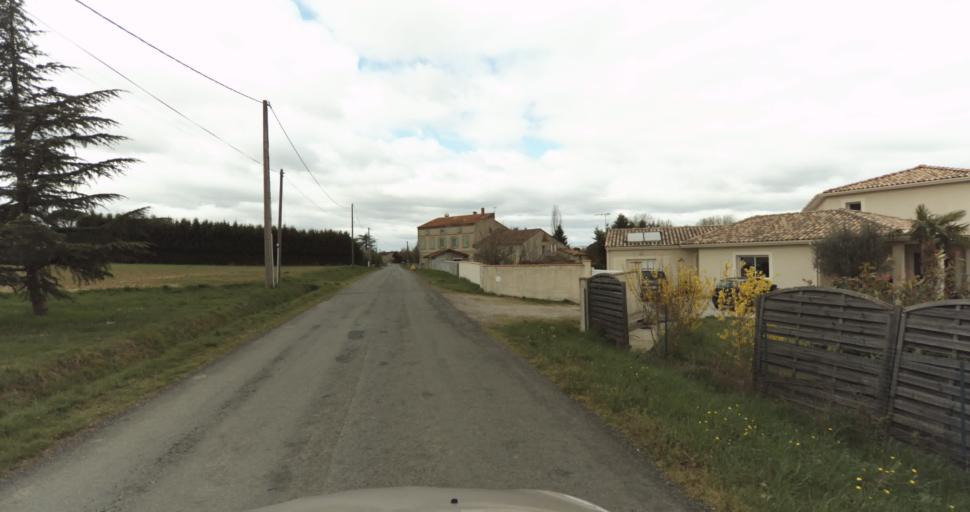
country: FR
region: Midi-Pyrenees
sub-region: Departement du Tarn
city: Puygouzon
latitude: 43.9079
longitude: 2.1695
